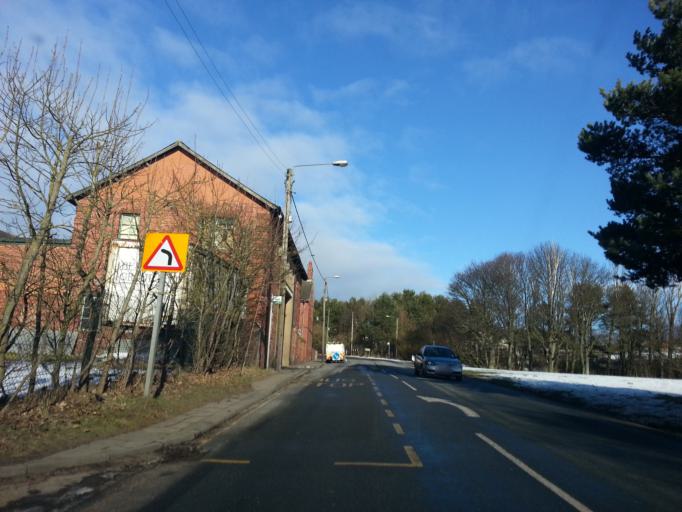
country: GB
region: England
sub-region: County Durham
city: Crook
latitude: 54.7237
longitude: -1.7496
